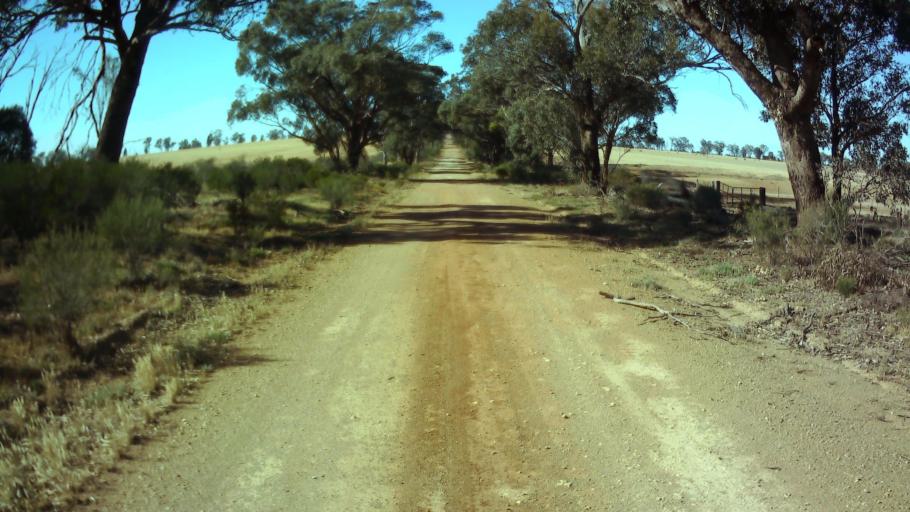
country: AU
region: New South Wales
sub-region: Weddin
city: Grenfell
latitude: -33.8922
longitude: 147.8802
